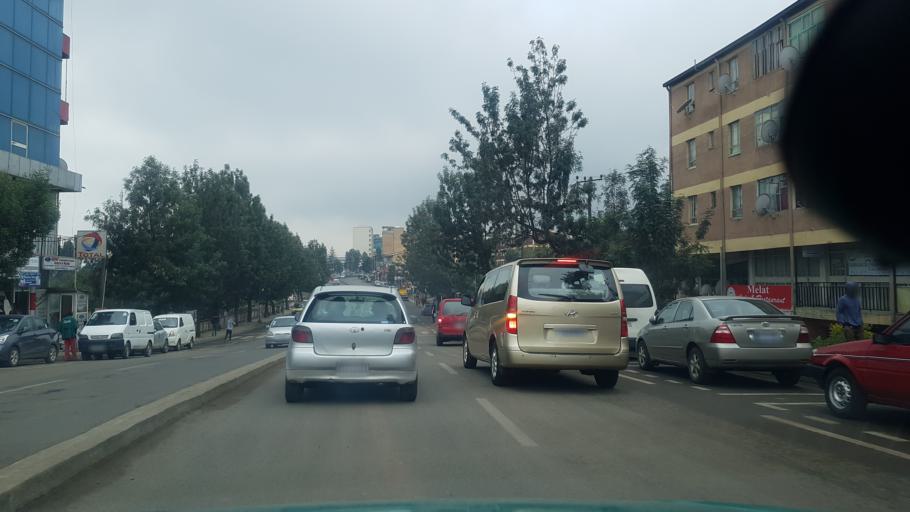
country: ET
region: Adis Abeba
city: Addis Ababa
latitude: 9.0213
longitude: 38.7922
